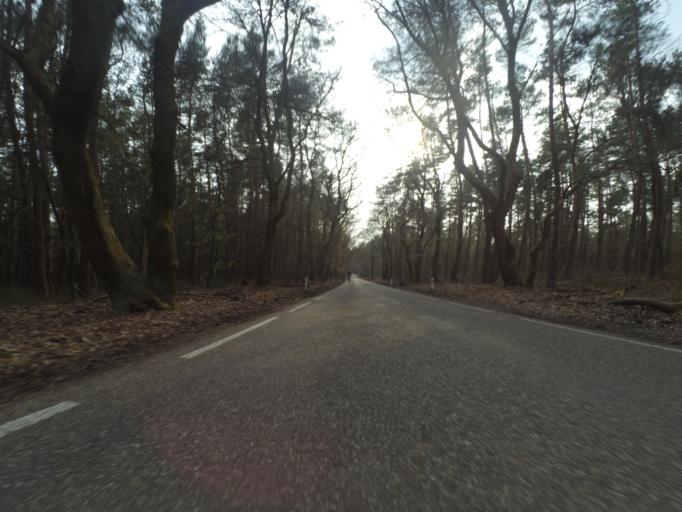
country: NL
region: Gelderland
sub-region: Gemeente Apeldoorn
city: Beekbergen
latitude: 52.1497
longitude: 5.9438
